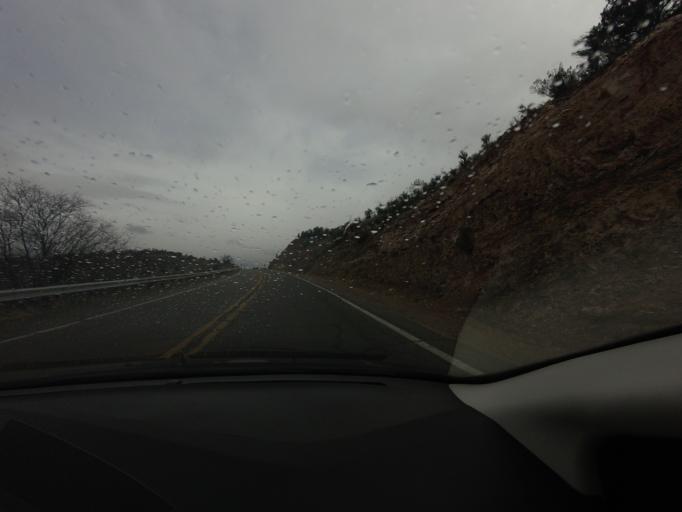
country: US
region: Arizona
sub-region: Yavapai County
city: Lake Montezuma
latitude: 34.6488
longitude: -111.8229
